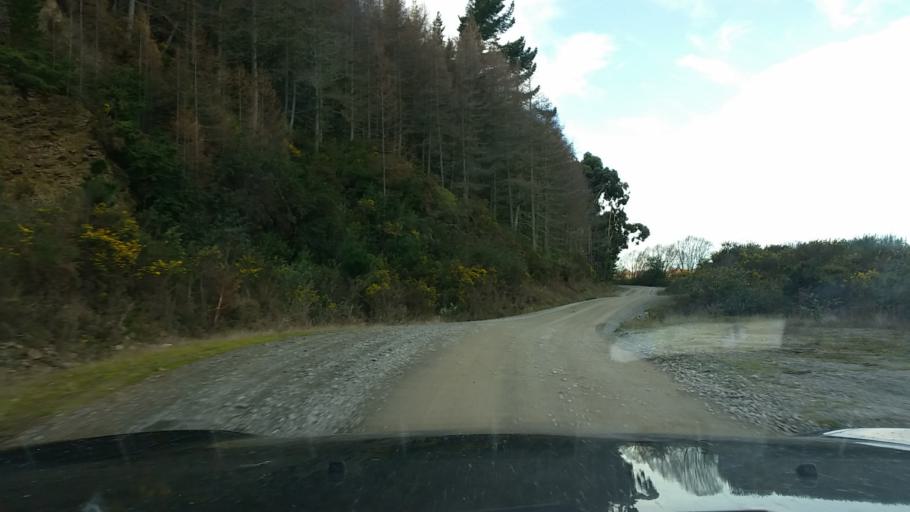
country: NZ
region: Nelson
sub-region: Nelson City
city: Nelson
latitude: -41.5748
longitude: 173.4424
